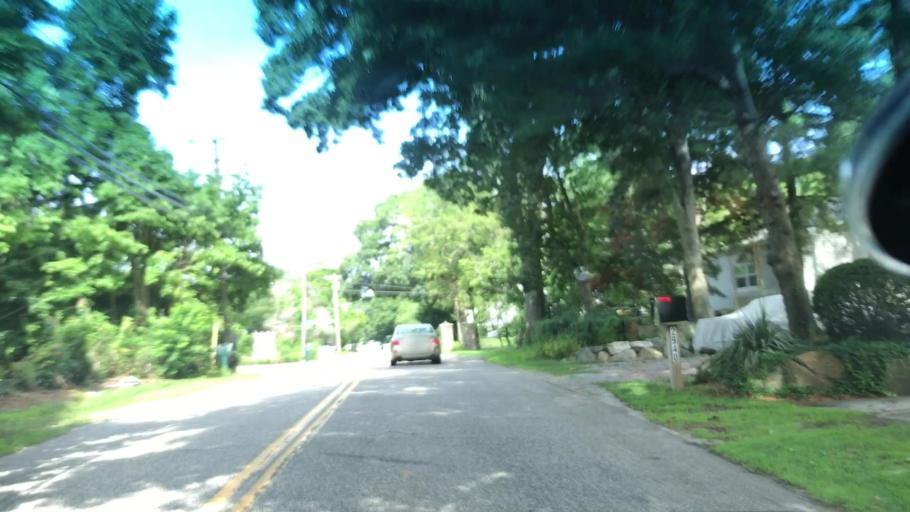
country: US
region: New York
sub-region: Suffolk County
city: Wading River
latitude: 40.9653
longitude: -72.8144
